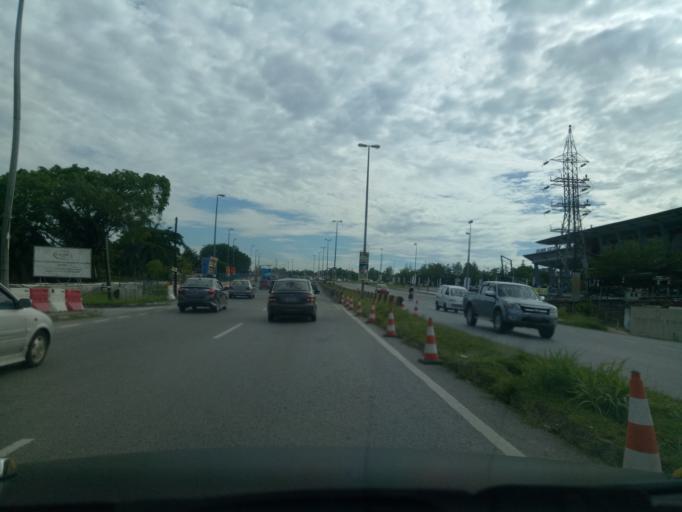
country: MY
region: Sarawak
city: Kuching
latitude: 1.4808
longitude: 110.3311
